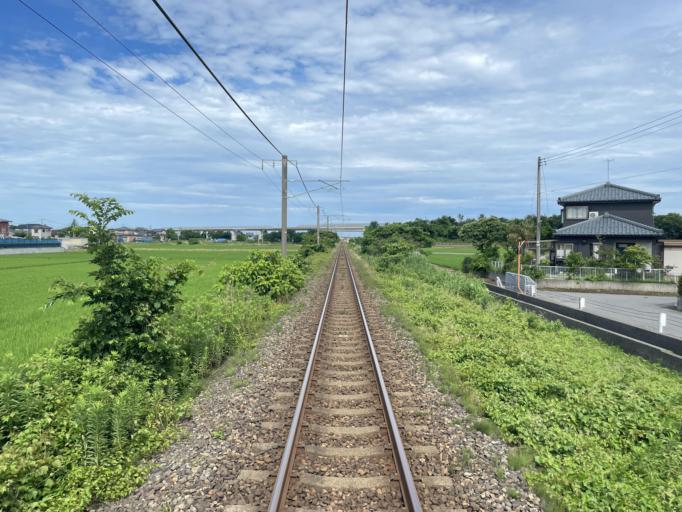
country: JP
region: Niigata
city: Suibara
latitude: 37.9163
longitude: 139.2038
